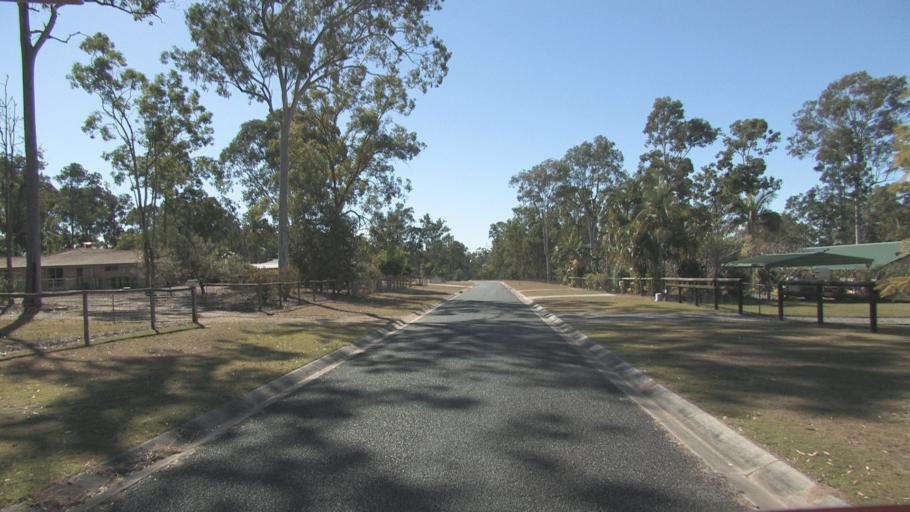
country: AU
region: Queensland
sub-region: Logan
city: North Maclean
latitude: -27.8231
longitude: 152.9458
